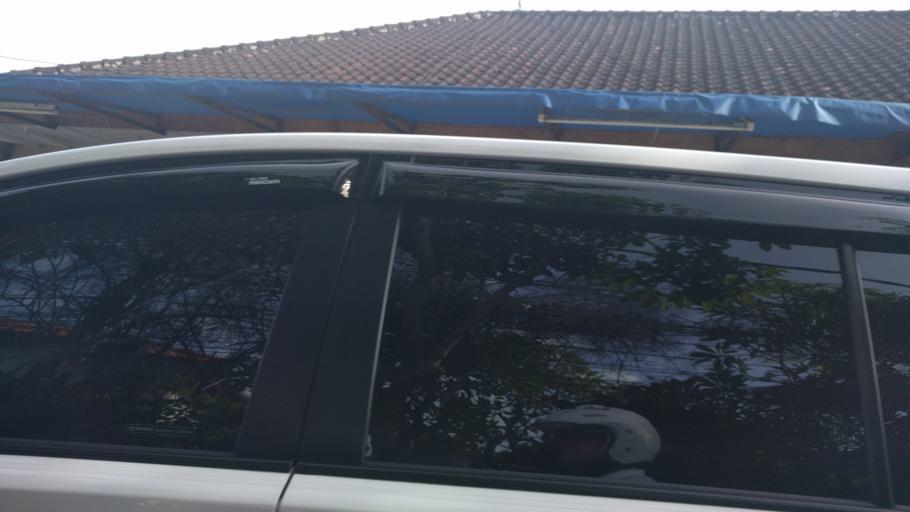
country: ID
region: Bali
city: Kuta
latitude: -8.7225
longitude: 115.1737
